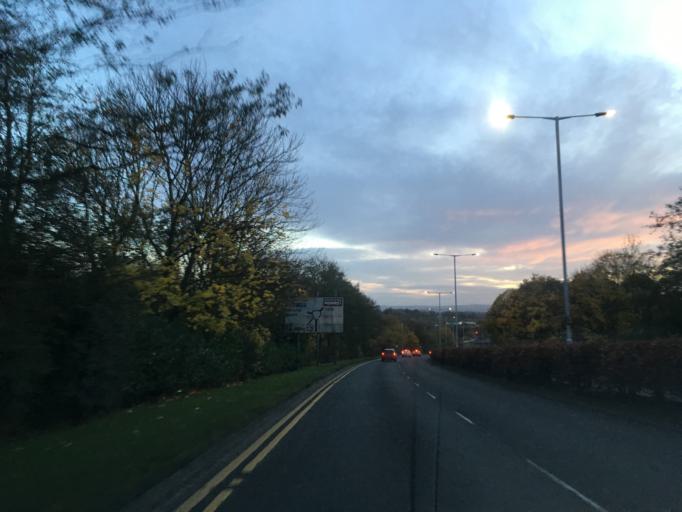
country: GB
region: Scotland
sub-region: Fife
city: Dunfermline
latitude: 56.0700
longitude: -3.4520
